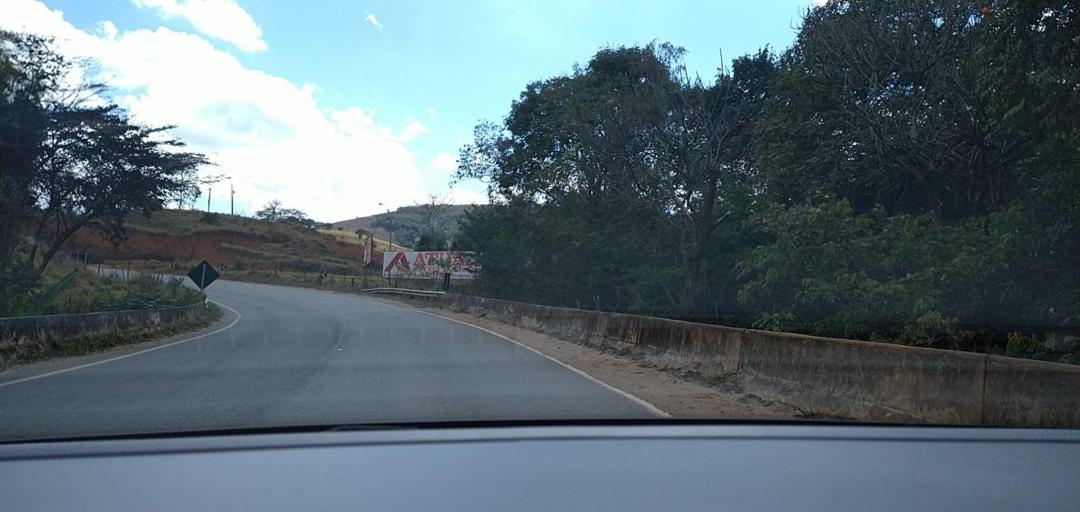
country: BR
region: Minas Gerais
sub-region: Ponte Nova
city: Ponte Nova
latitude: -20.4329
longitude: -42.8901
